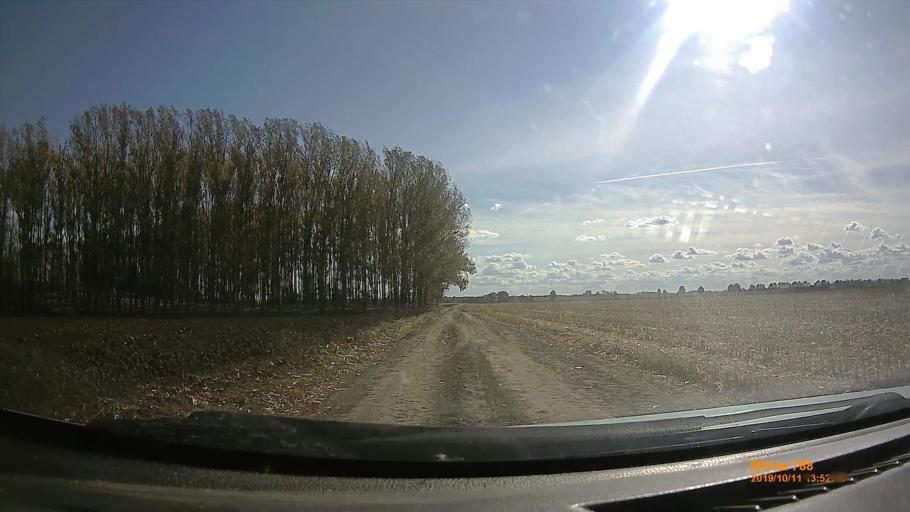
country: HU
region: Hajdu-Bihar
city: Hajduszoboszlo
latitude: 47.5397
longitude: 21.4009
